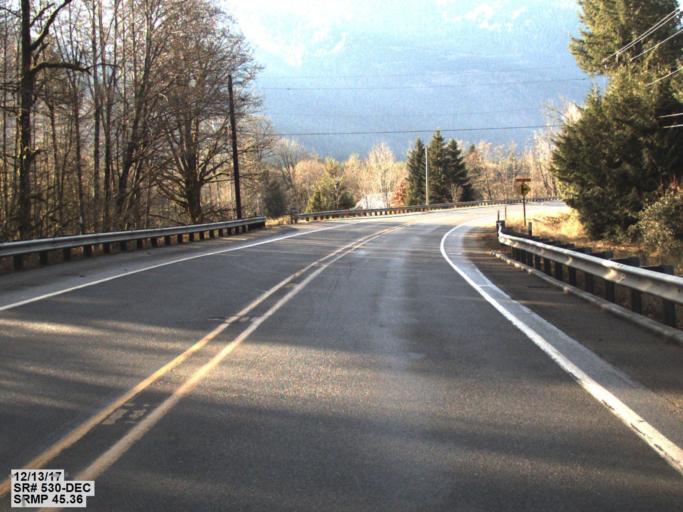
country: US
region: Washington
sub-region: Snohomish County
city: Darrington
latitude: 48.2699
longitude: -121.6716
